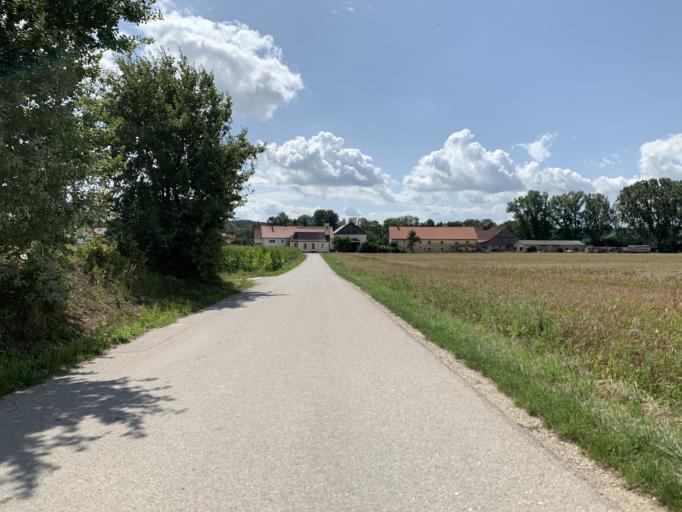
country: DE
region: Bavaria
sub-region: Upper Bavaria
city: Zolling
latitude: 48.4529
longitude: 11.7587
